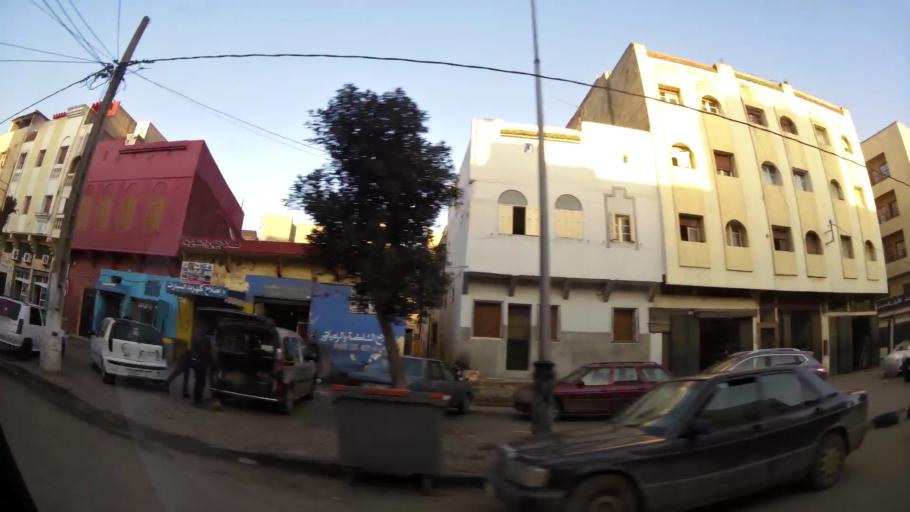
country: MA
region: Chaouia-Ouardigha
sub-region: Settat Province
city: Settat
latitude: 32.9983
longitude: -7.6165
